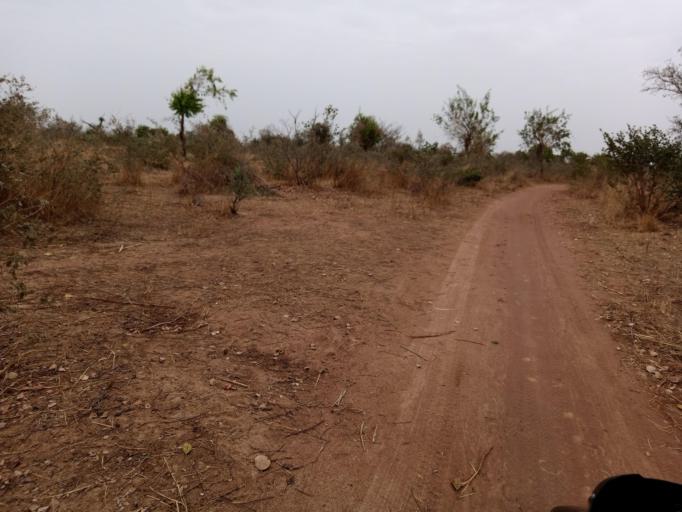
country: BF
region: Boucle du Mouhoun
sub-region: Province de la Kossi
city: Nouna
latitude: 12.8460
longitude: -4.0779
